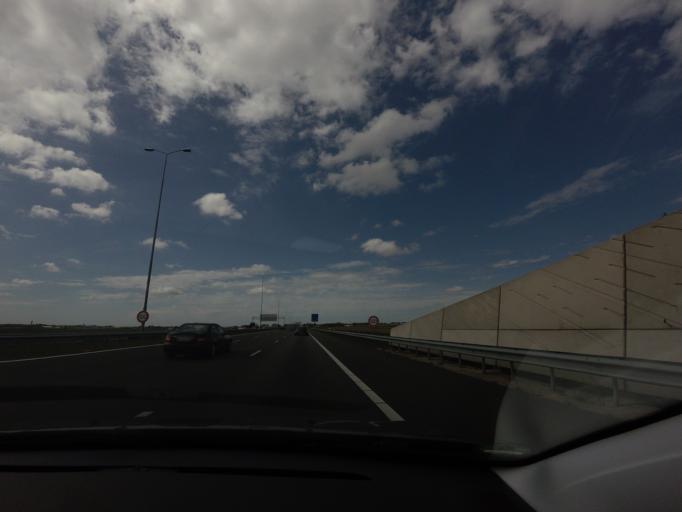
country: NL
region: North Holland
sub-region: Gemeente Aalsmeer
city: Aalsmeer
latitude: 52.3314
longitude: 4.7667
